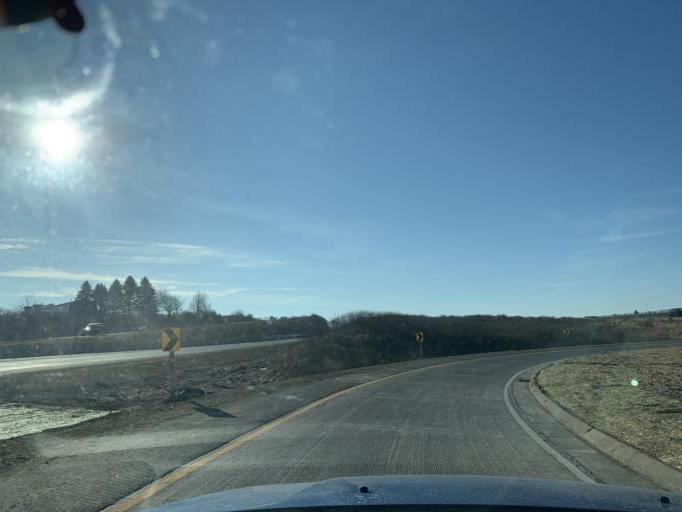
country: US
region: Wisconsin
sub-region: Iowa County
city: Dodgeville
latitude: 42.9345
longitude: -90.1319
